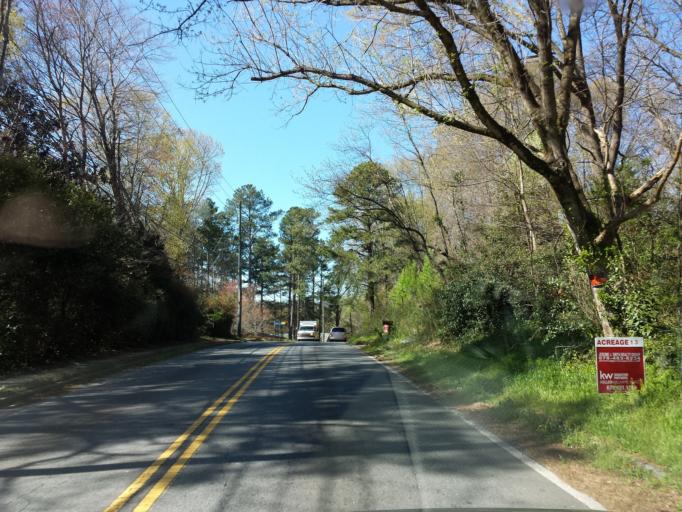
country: US
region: Georgia
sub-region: Cobb County
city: Fair Oaks
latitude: 33.9180
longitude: -84.5551
